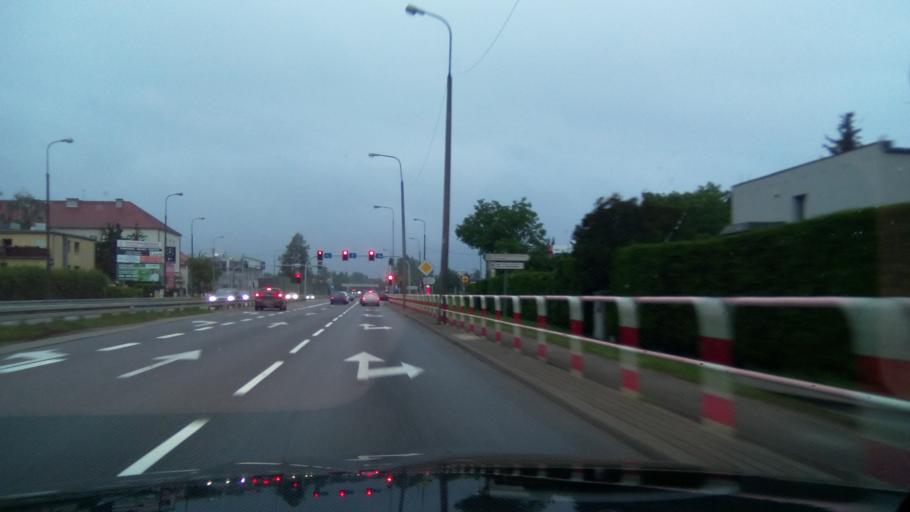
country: PL
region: Greater Poland Voivodeship
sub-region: Powiat poznanski
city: Swarzedz
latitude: 52.4066
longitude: 17.0859
